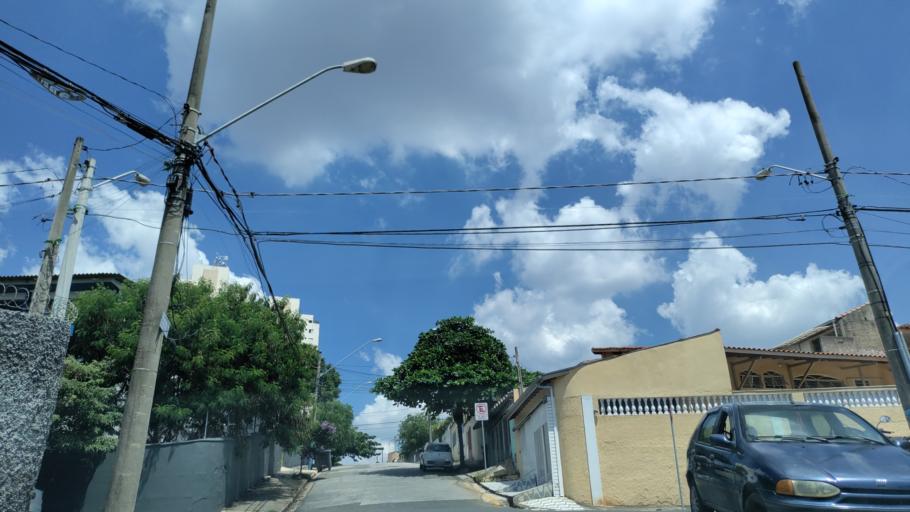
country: BR
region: Sao Paulo
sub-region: Sorocaba
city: Sorocaba
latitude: -23.4907
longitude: -47.4680
